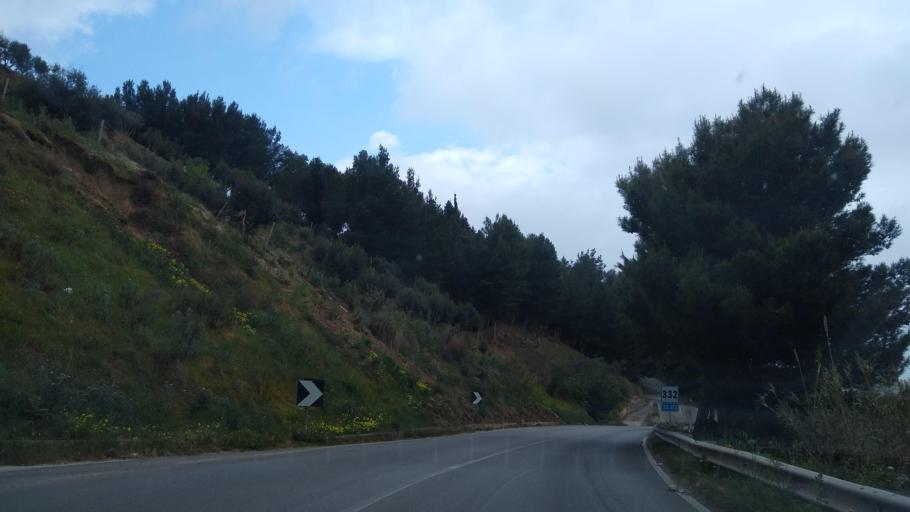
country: IT
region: Sicily
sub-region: Trapani
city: Alcamo
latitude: 37.9769
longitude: 12.9392
